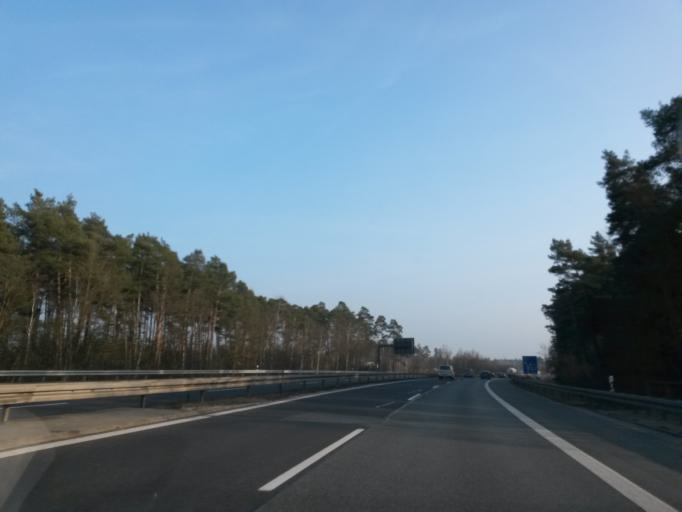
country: DE
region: Bavaria
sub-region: Regierungsbezirk Mittelfranken
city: Feucht
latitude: 49.3619
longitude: 11.1992
